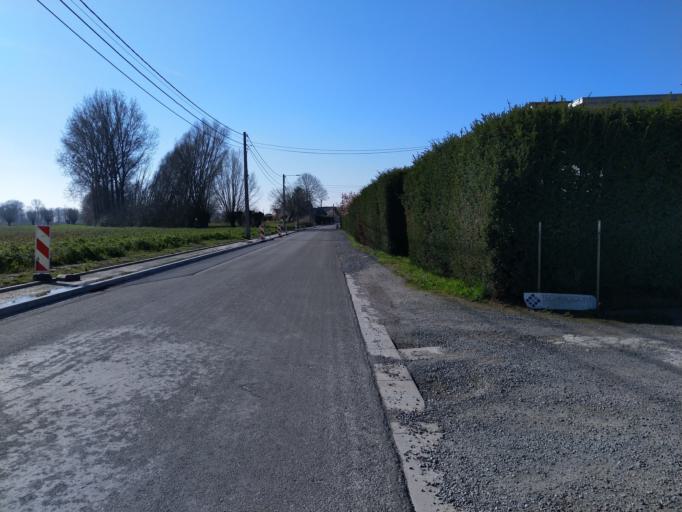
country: BE
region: Wallonia
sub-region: Province du Hainaut
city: Soignies
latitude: 50.5388
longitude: 4.0074
